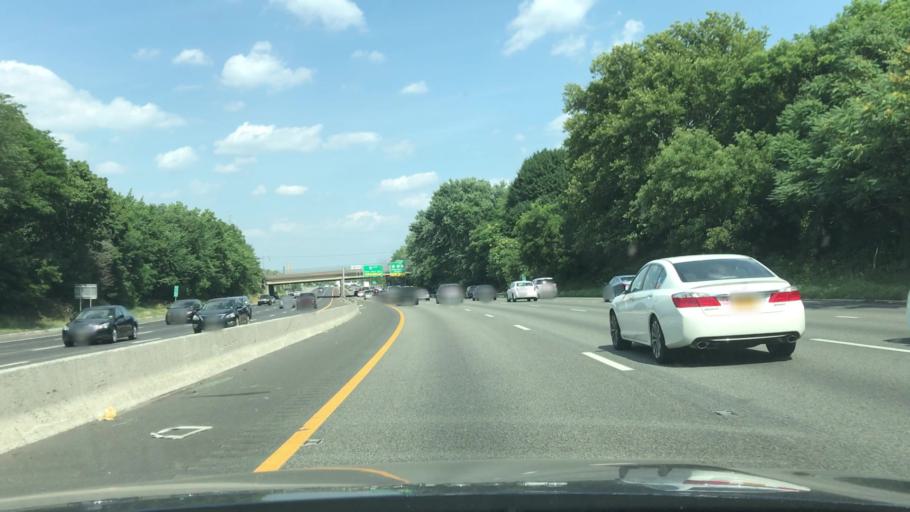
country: US
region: New Jersey
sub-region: Bergen County
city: Elmwood Park
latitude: 40.8992
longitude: -74.1475
